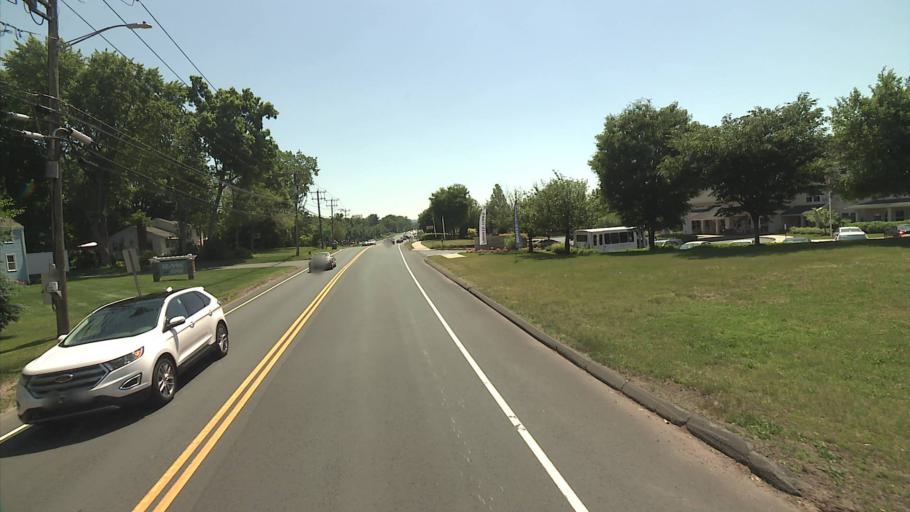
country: US
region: Connecticut
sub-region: Hartford County
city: Manchester
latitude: 41.8147
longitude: -72.5294
